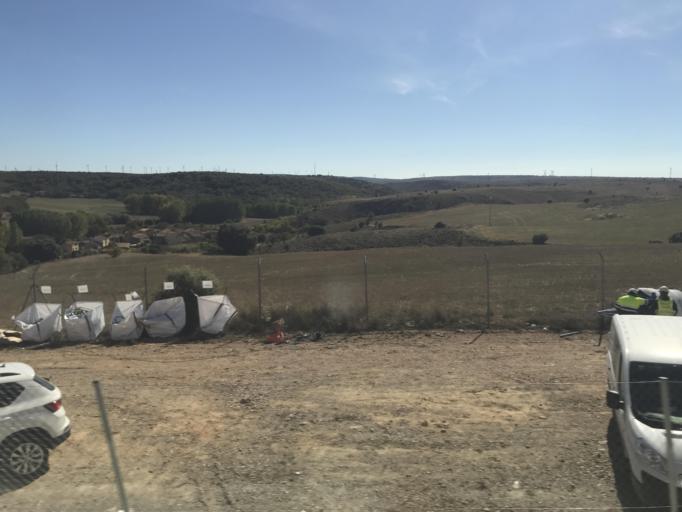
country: ES
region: Castille and Leon
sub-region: Provincia de Soria
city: Medinaceli
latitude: 41.1288
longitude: -2.3380
